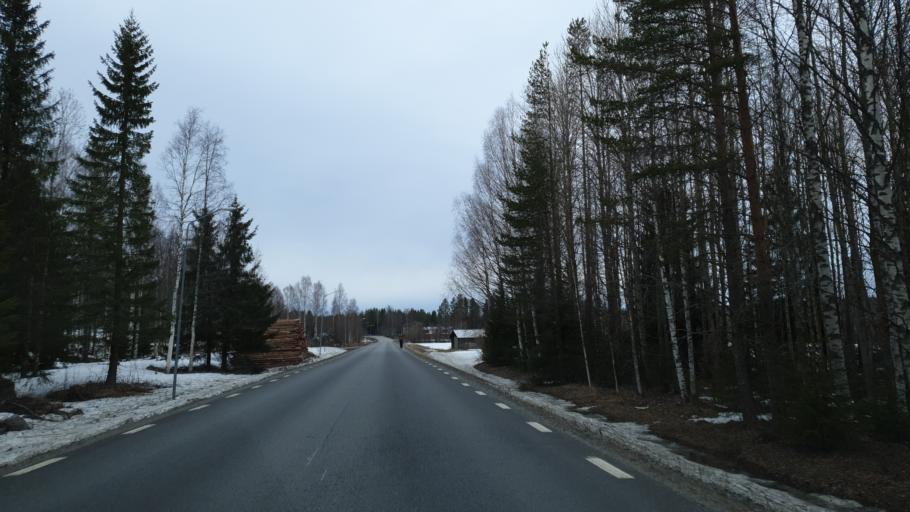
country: SE
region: Vaesterbotten
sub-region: Robertsfors Kommun
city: Robertsfors
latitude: 64.3880
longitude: 20.8965
